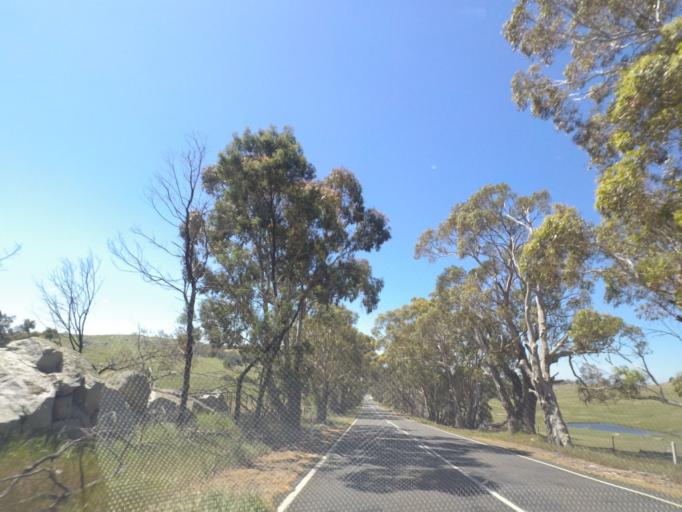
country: AU
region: Victoria
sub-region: Hume
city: Sunbury
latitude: -37.1777
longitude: 144.7469
